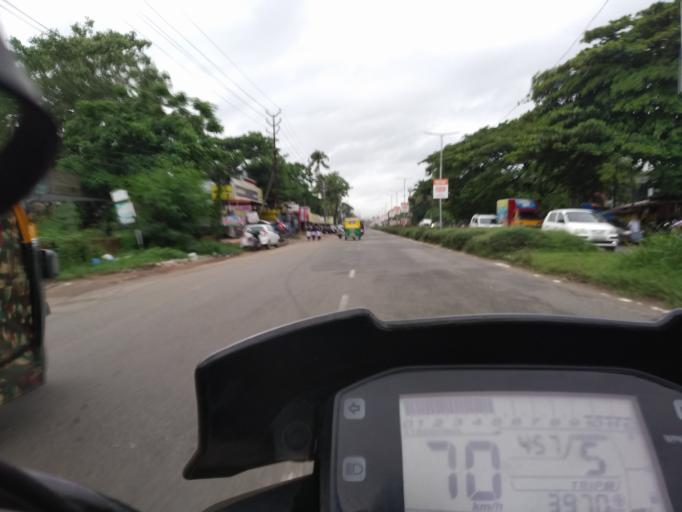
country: IN
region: Kerala
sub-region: Alappuzha
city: Arukutti
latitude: 9.8721
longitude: 76.3046
